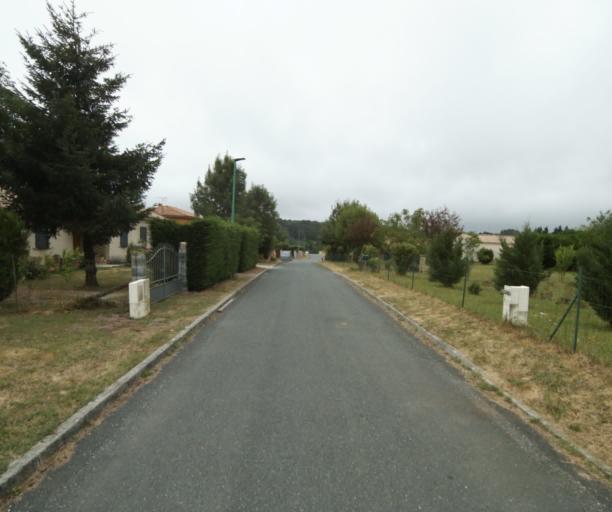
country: FR
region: Midi-Pyrenees
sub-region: Departement du Tarn
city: Soreze
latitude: 43.4063
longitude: 2.0784
